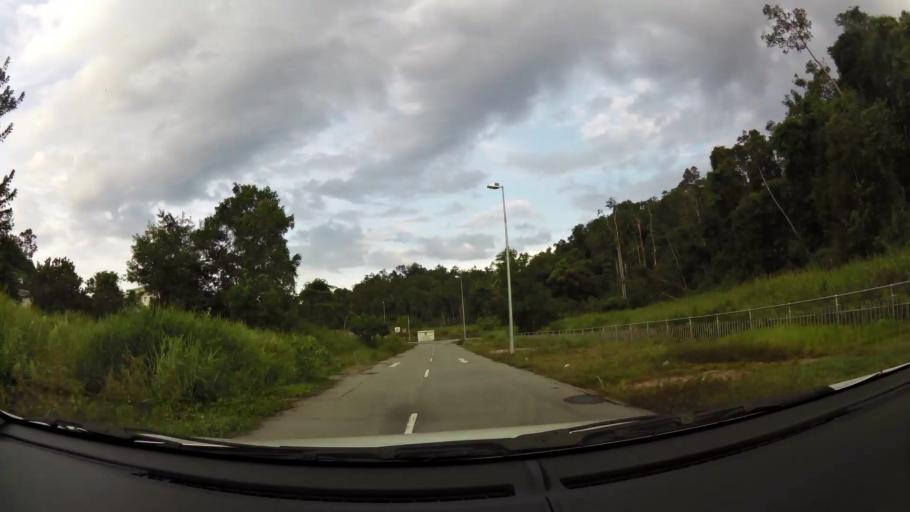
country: BN
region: Brunei and Muara
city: Bandar Seri Begawan
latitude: 4.9492
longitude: 114.9786
